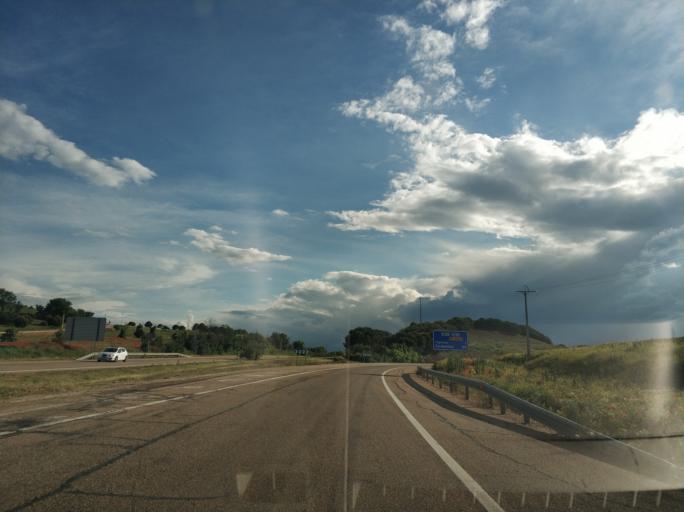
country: ES
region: Castille and Leon
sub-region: Provincia de Valladolid
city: Arroyo
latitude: 41.6172
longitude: -4.7872
